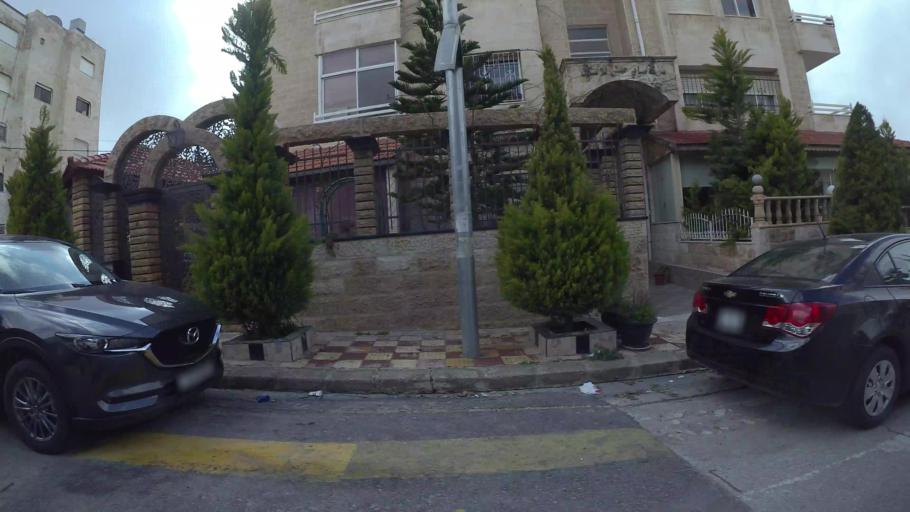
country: JO
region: Amman
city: Al Jubayhah
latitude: 31.9869
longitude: 35.8464
